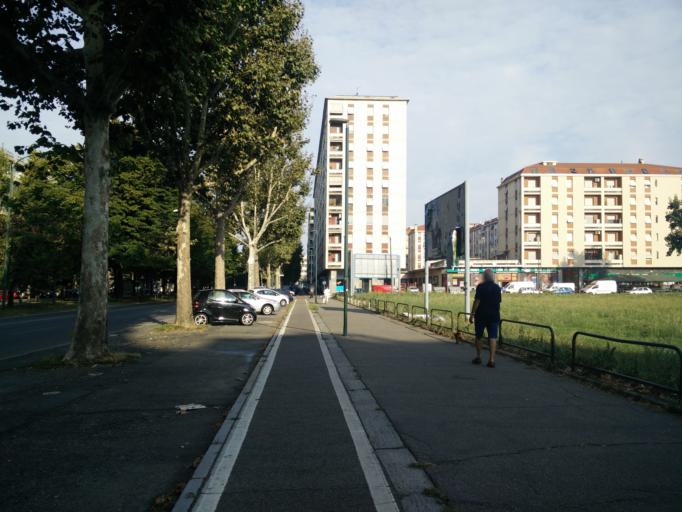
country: IT
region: Piedmont
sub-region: Provincia di Torino
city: Nichelino
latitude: 45.0246
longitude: 7.6434
